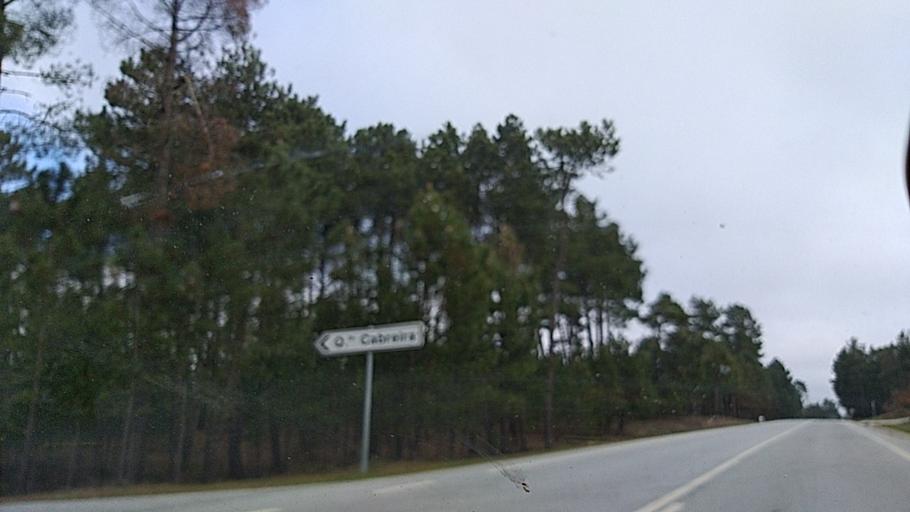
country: PT
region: Guarda
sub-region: Aguiar da Beira
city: Aguiar da Beira
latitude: 40.7514
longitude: -7.5049
